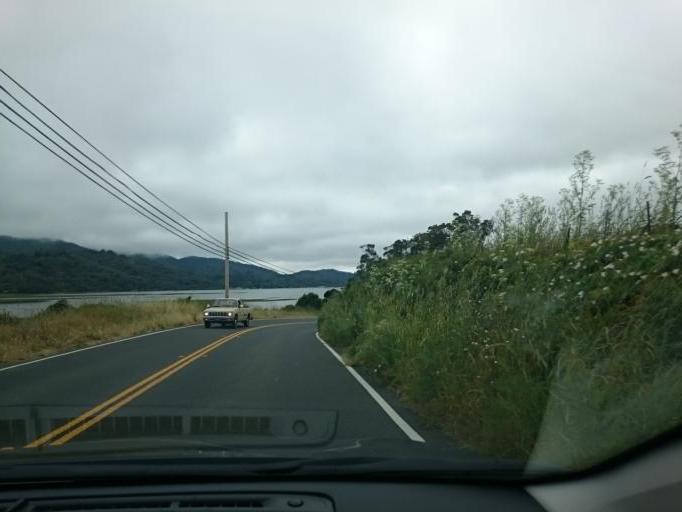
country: US
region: California
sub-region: Marin County
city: Inverness
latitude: 38.0913
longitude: -122.8243
